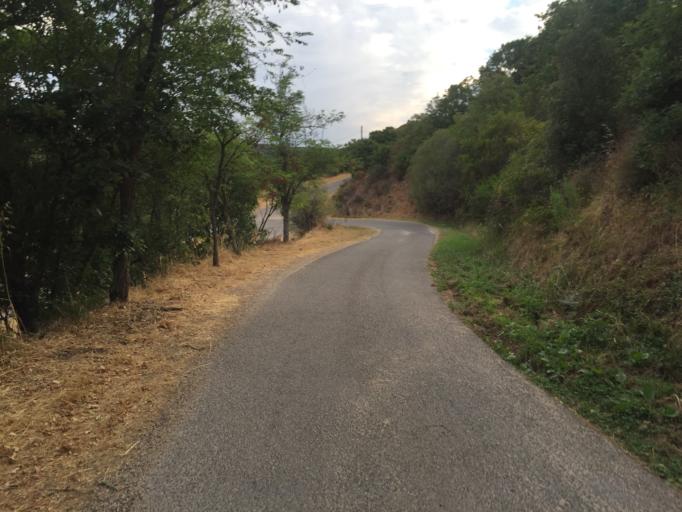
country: IT
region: Sardinia
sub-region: Provincia di Olbia-Tempio
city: Aggius
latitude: 40.9265
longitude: 9.0732
